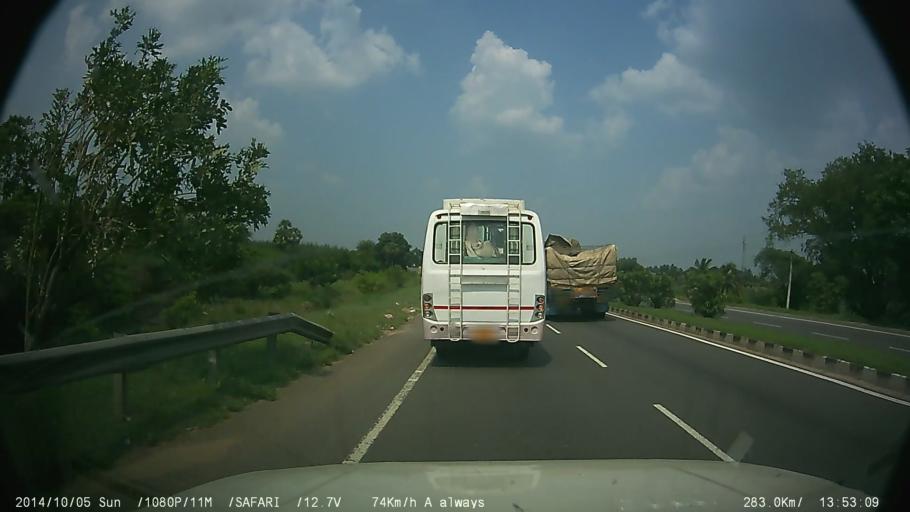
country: IN
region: Tamil Nadu
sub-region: Villupuram
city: Vikravandi
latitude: 12.1002
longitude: 79.5670
